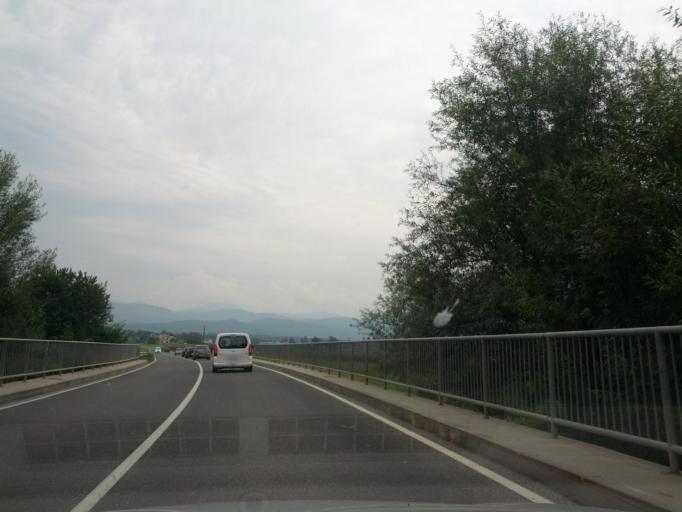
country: SI
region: Domzale
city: Vir
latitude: 46.1436
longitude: 14.6159
